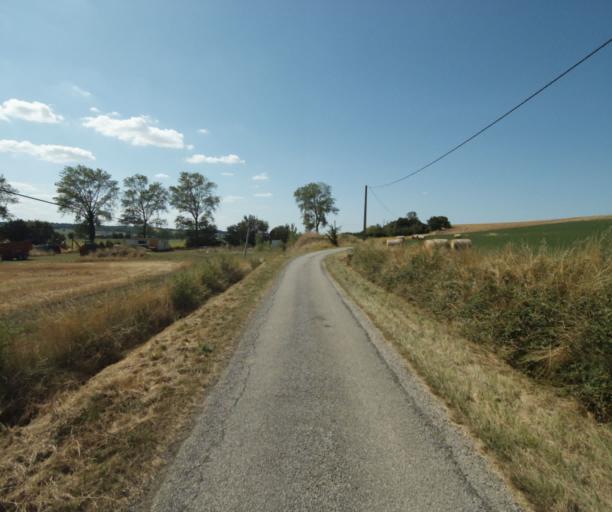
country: FR
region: Midi-Pyrenees
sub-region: Departement de la Haute-Garonne
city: Saint-Felix-Lauragais
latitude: 43.4777
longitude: 1.9002
